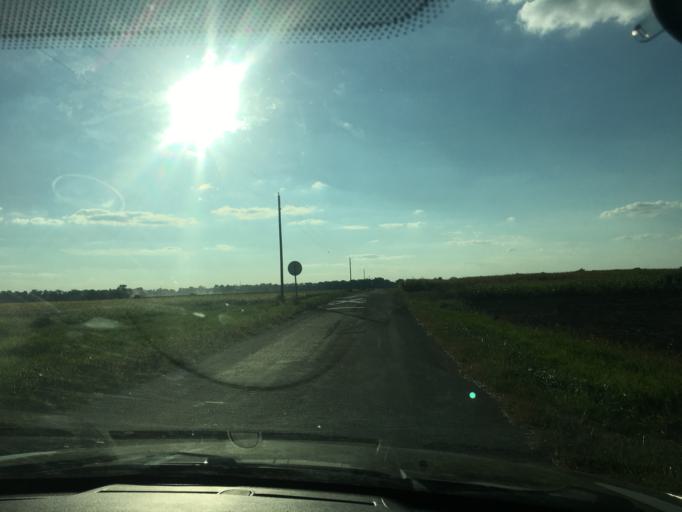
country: US
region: Ohio
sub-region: Champaign County
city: Urbana
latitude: 40.1717
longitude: -83.7762
